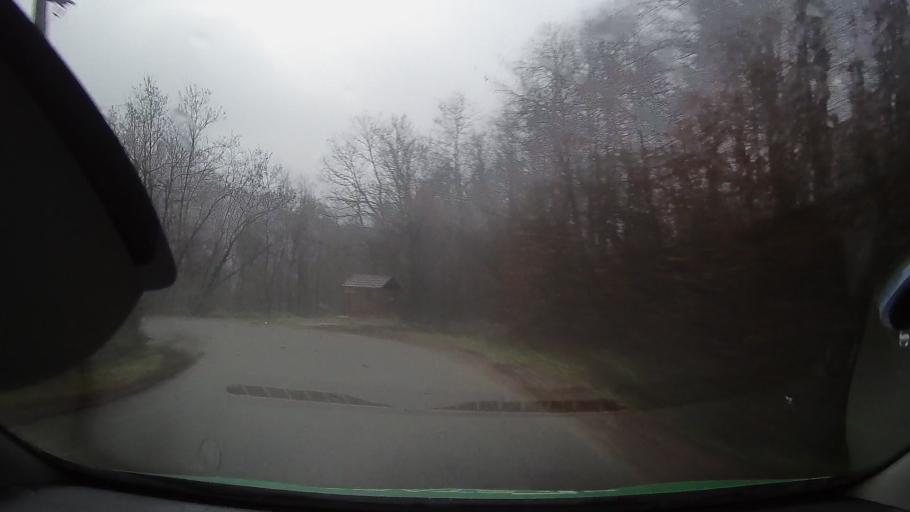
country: RO
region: Hunedoara
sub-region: Comuna Ribita
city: Ribita
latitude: 46.2463
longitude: 22.7509
